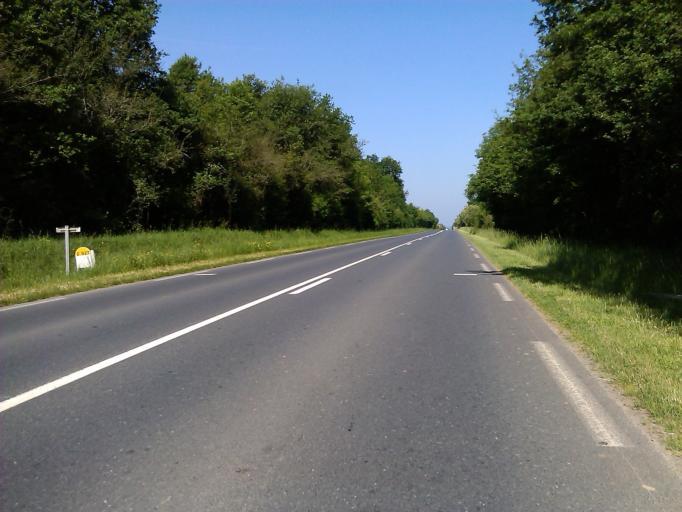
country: FR
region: Centre
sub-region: Departement de l'Indre
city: Cluis
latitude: 46.6028
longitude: 1.7202
